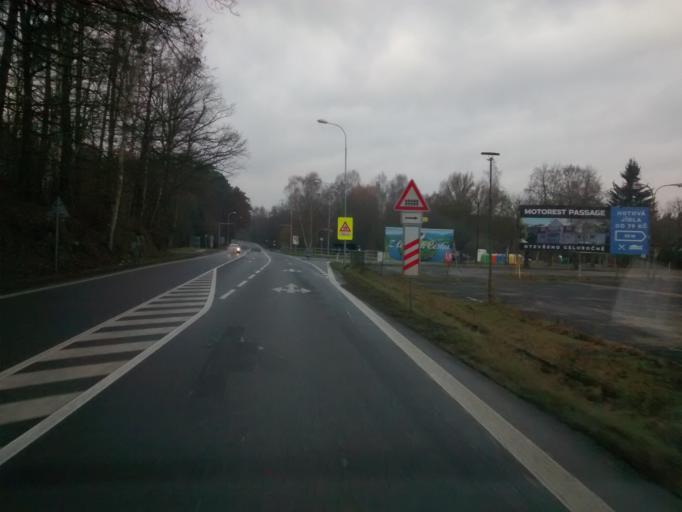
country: CZ
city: Doksy
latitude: 50.5848
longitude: 14.6298
